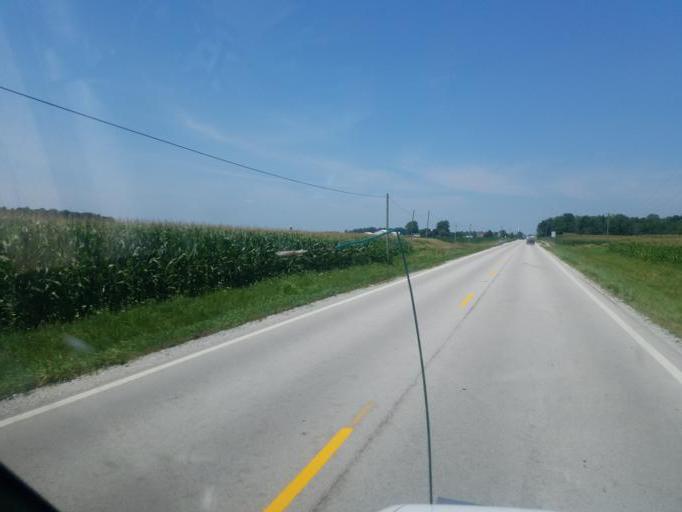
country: US
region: Ohio
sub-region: Shelby County
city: Fort Loramie
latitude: 40.3590
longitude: -84.4342
